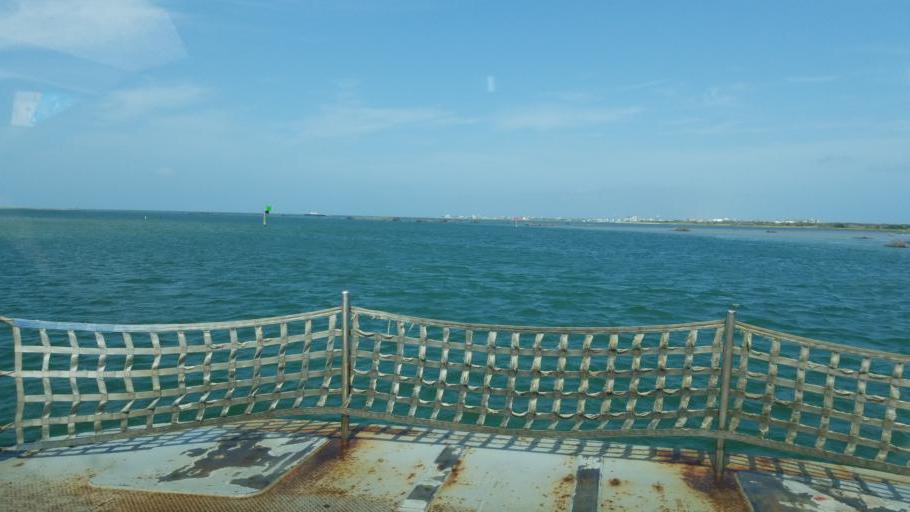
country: US
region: North Carolina
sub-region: Dare County
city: Buxton
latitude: 35.2045
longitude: -75.7249
